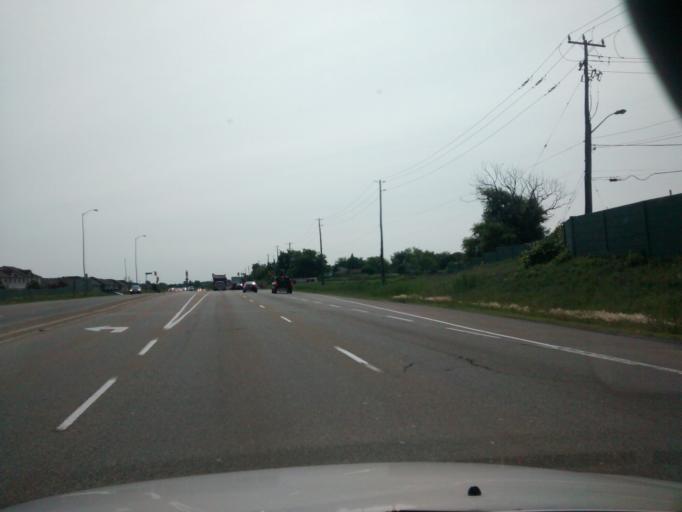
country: CA
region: Ontario
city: Hamilton
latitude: 43.1963
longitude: -79.8092
